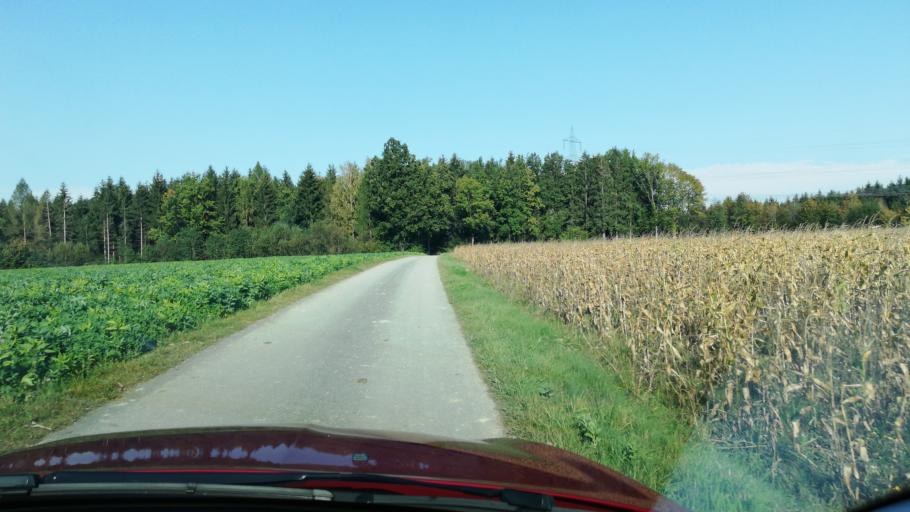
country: AT
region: Upper Austria
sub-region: Politischer Bezirk Kirchdorf an der Krems
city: Kremsmunster
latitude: 48.0989
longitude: 14.1585
